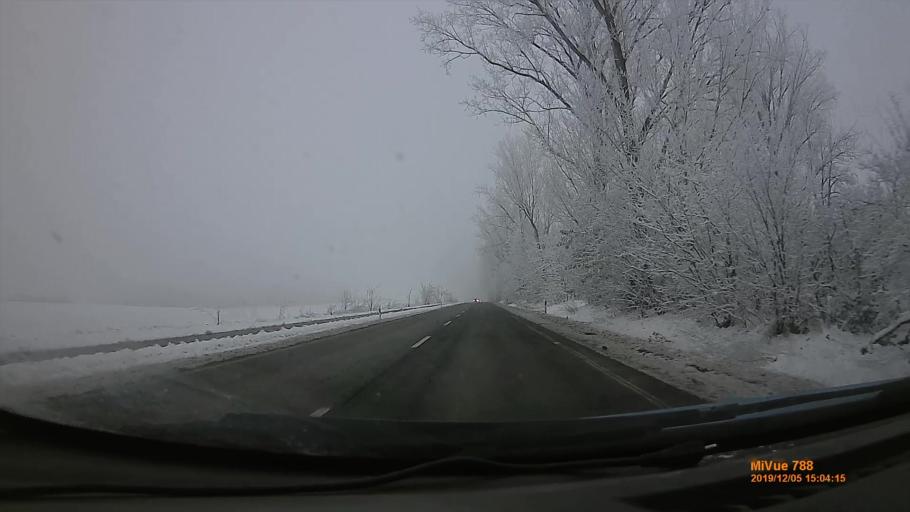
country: HU
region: Szabolcs-Szatmar-Bereg
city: Tiszanagyfalu
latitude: 48.0942
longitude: 21.4941
